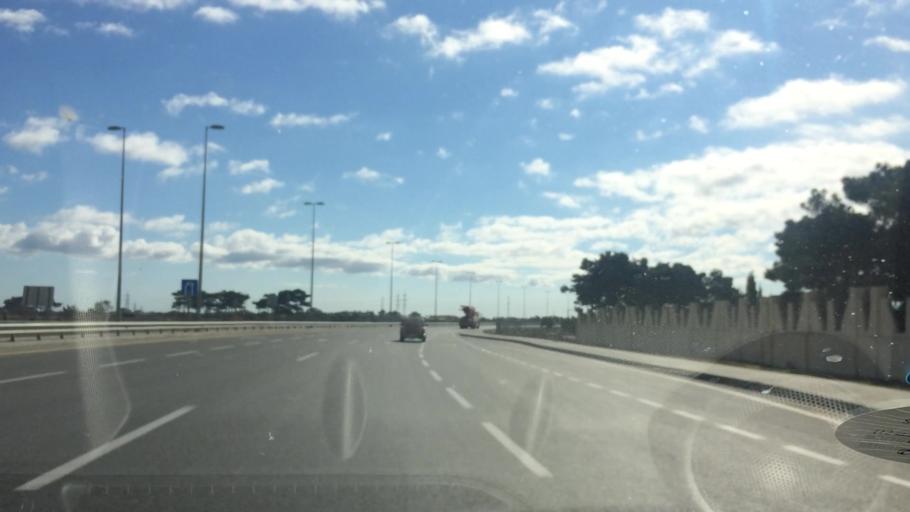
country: AZ
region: Baki
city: Qala
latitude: 40.4425
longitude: 50.1796
